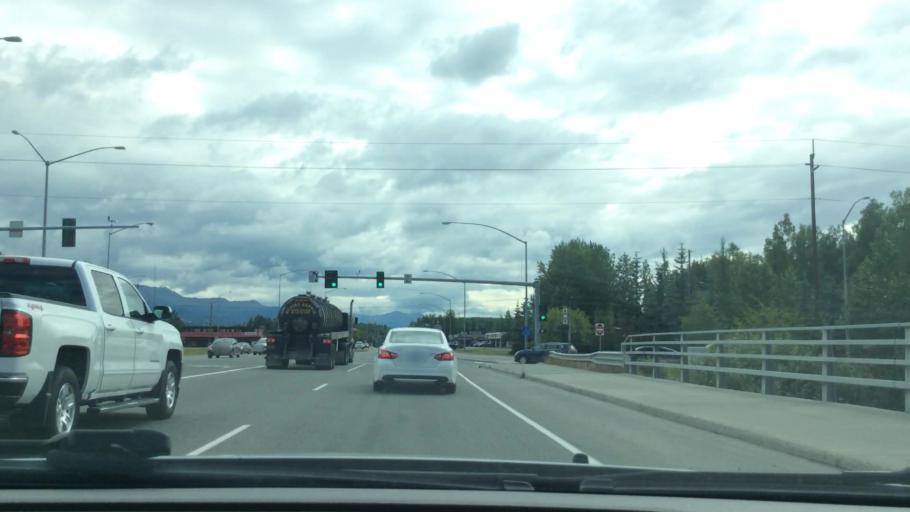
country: US
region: Alaska
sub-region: Anchorage Municipality
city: Anchorage
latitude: 61.2248
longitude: -149.7786
